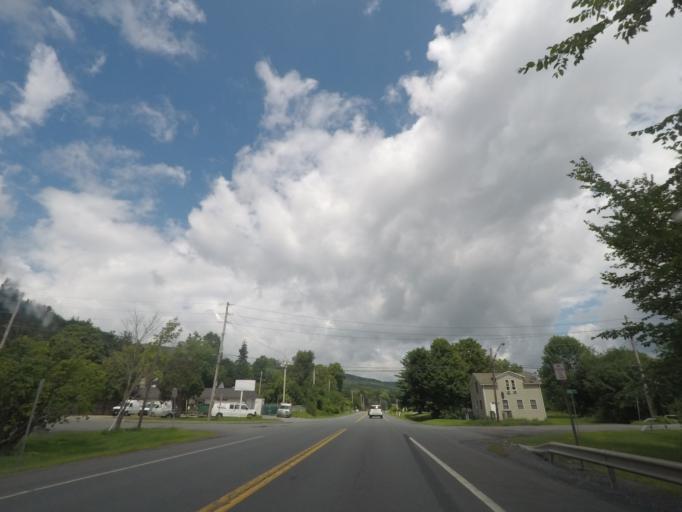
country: US
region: Massachusetts
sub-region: Berkshire County
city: Williamstown
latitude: 42.6912
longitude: -73.3704
